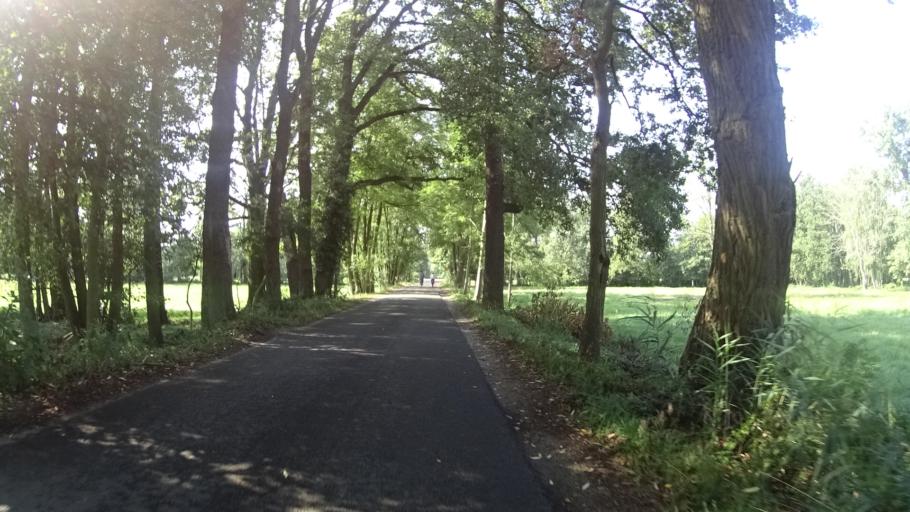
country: DE
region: Brandenburg
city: Straupitz
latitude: 51.8740
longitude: 14.1181
